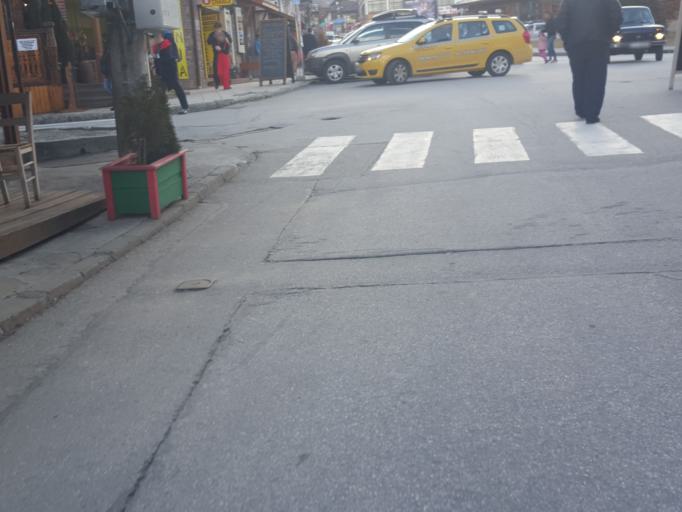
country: BG
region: Blagoevgrad
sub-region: Obshtina Bansko
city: Bansko
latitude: 41.8305
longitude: 23.4814
